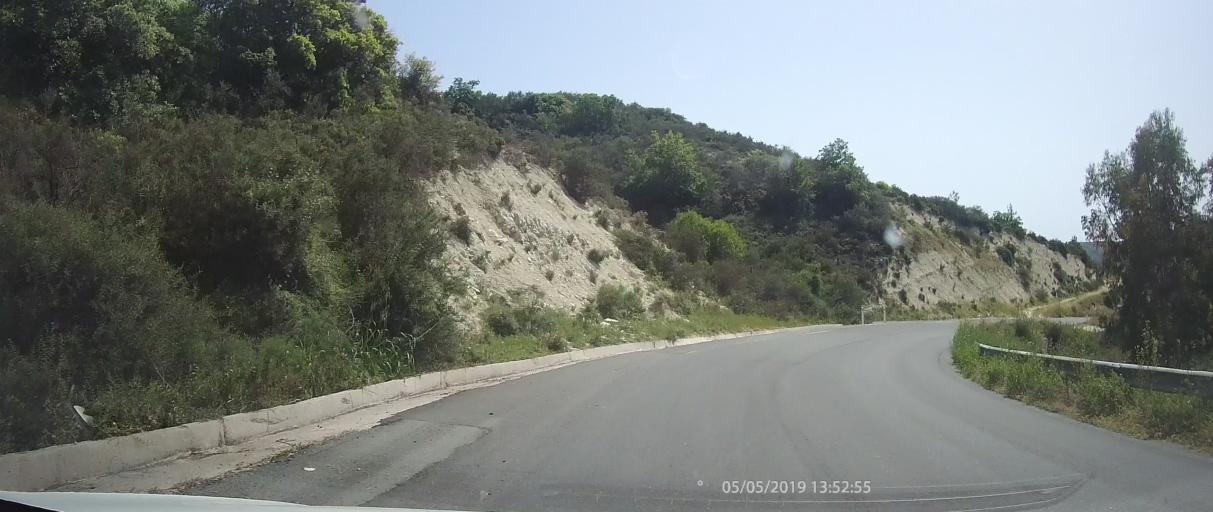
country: CY
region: Limassol
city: Pachna
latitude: 34.8263
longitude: 32.7270
